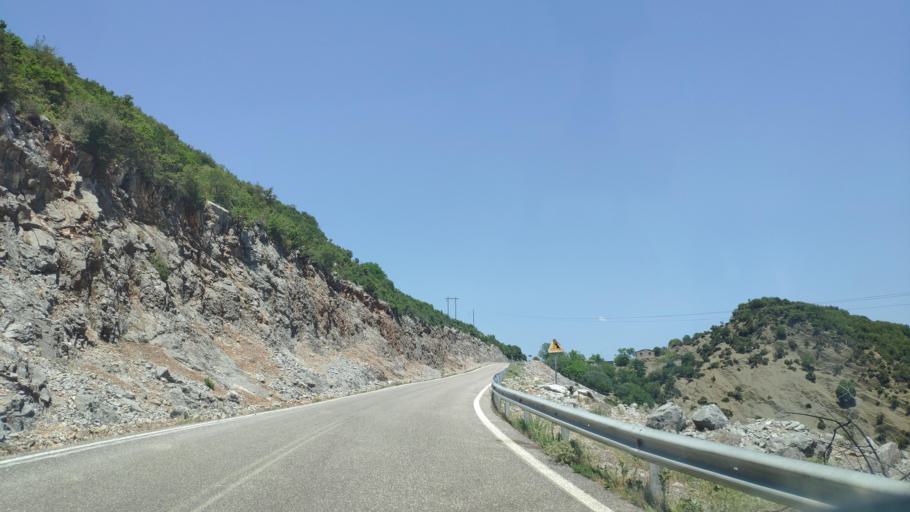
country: GR
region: Central Greece
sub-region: Nomos Evrytanias
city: Kerasochori
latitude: 39.1020
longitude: 21.4102
